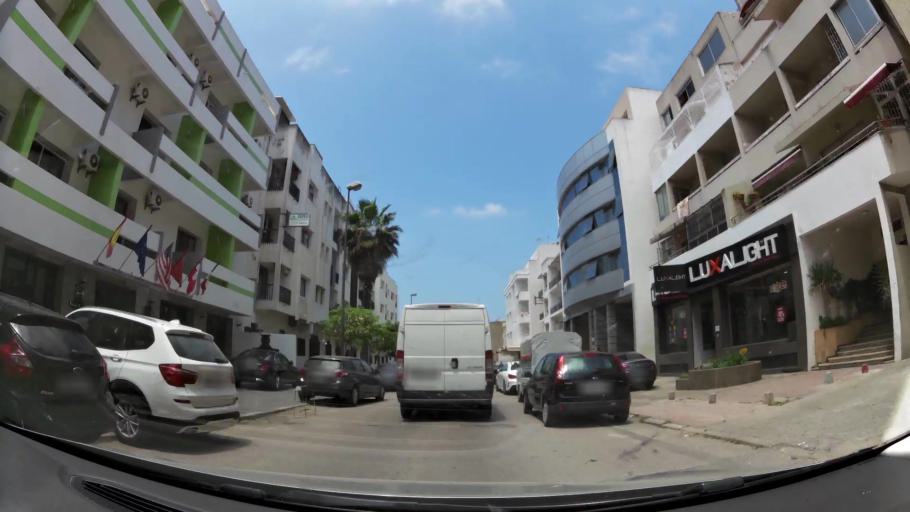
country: MA
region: Rabat-Sale-Zemmour-Zaer
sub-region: Rabat
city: Rabat
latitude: 34.0057
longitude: -6.8473
